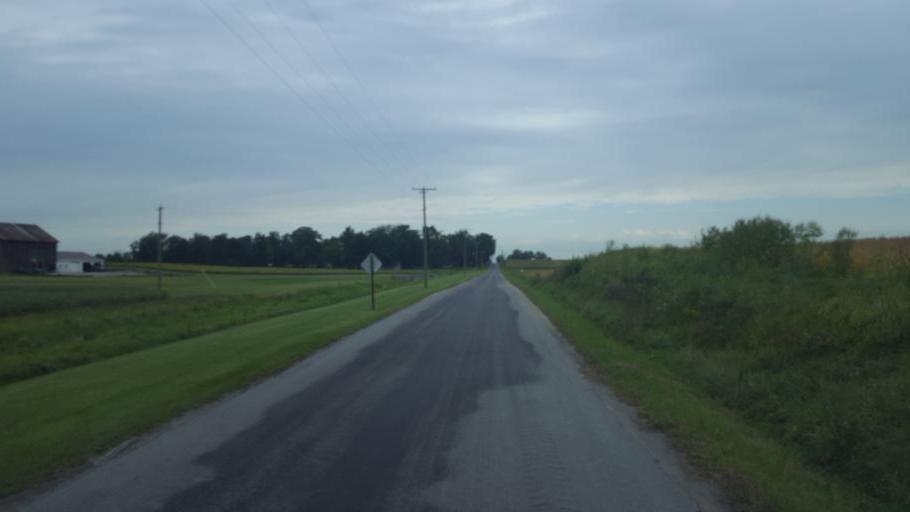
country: US
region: Ohio
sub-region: Wyandot County
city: Upper Sandusky
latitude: 40.8427
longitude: -83.1890
